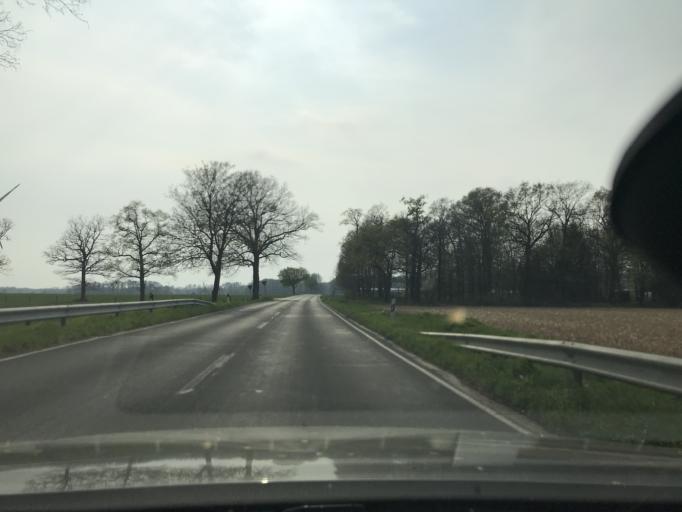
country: DE
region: North Rhine-Westphalia
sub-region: Regierungsbezirk Dusseldorf
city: Wachtendonk
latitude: 51.4393
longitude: 6.3337
